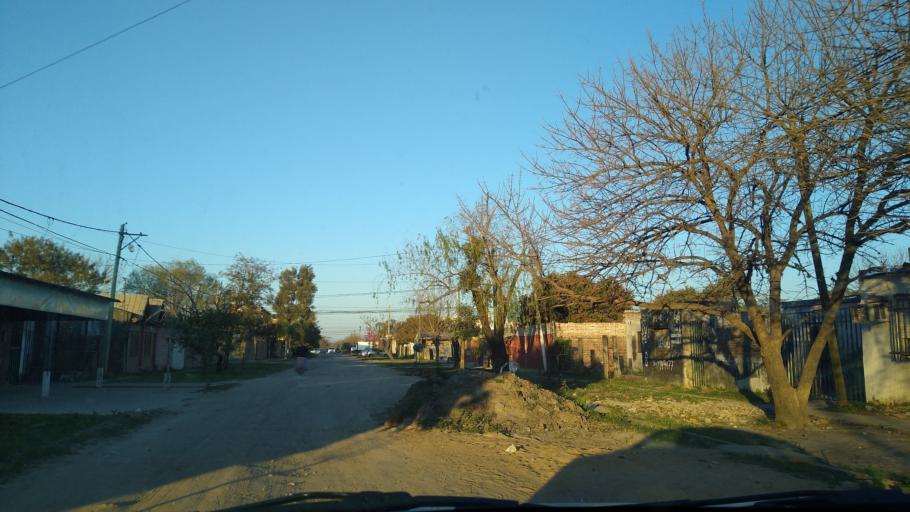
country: AR
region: Chaco
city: Resistencia
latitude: -27.4770
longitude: -58.9691
